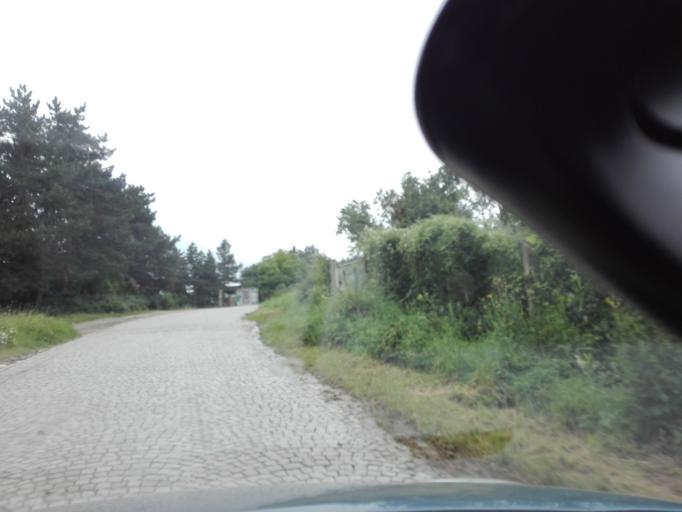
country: BG
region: Sofia-Capital
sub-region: Stolichna Obshtina
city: Sofia
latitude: 42.6042
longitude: 23.3990
